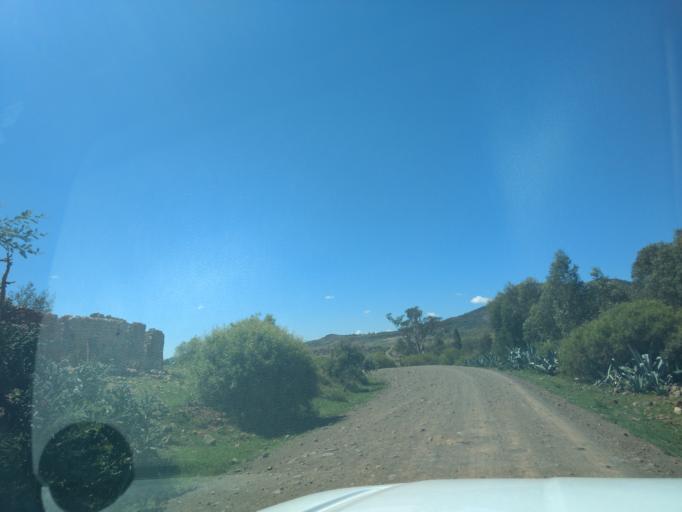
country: LS
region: Maseru
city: Maseru
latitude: -29.4880
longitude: 27.3715
